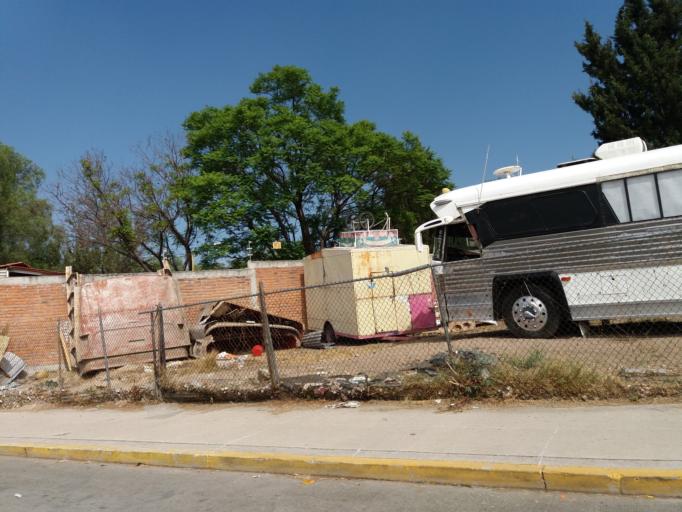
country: MX
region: Aguascalientes
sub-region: Aguascalientes
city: La Loma de los Negritos
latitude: 21.8699
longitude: -102.3166
